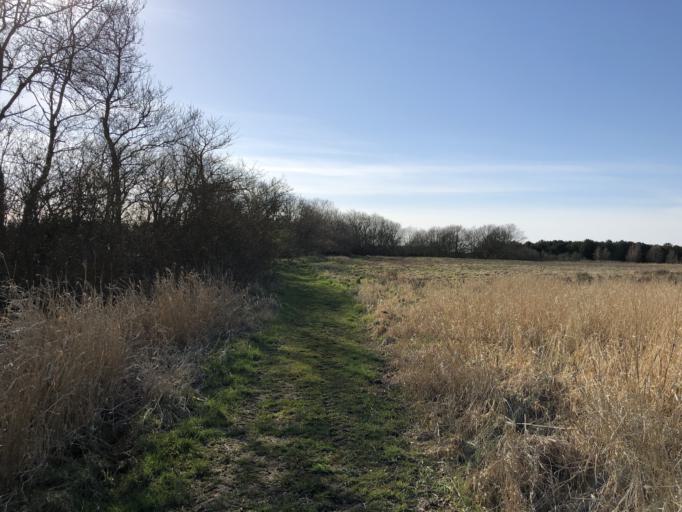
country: DK
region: Central Jutland
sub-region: Holstebro Kommune
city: Ulfborg
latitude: 56.3228
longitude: 8.3242
